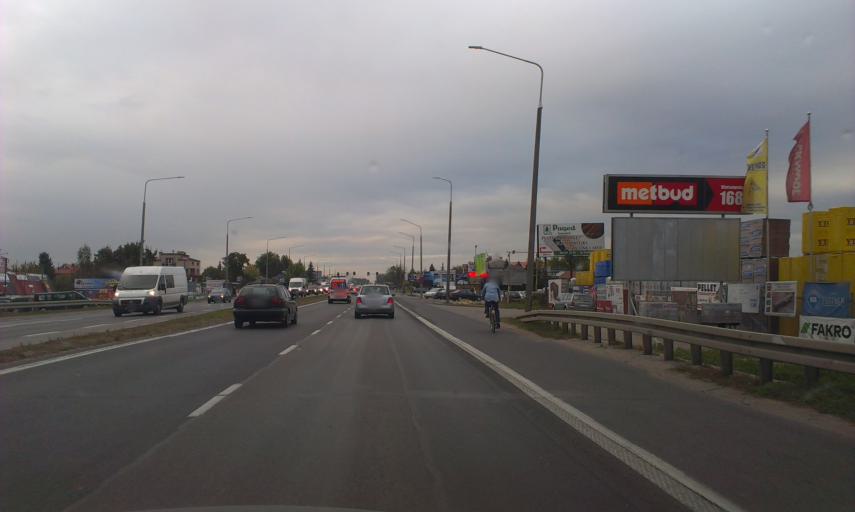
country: PL
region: Masovian Voivodeship
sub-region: Radom
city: Radom
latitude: 51.4398
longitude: 21.1464
